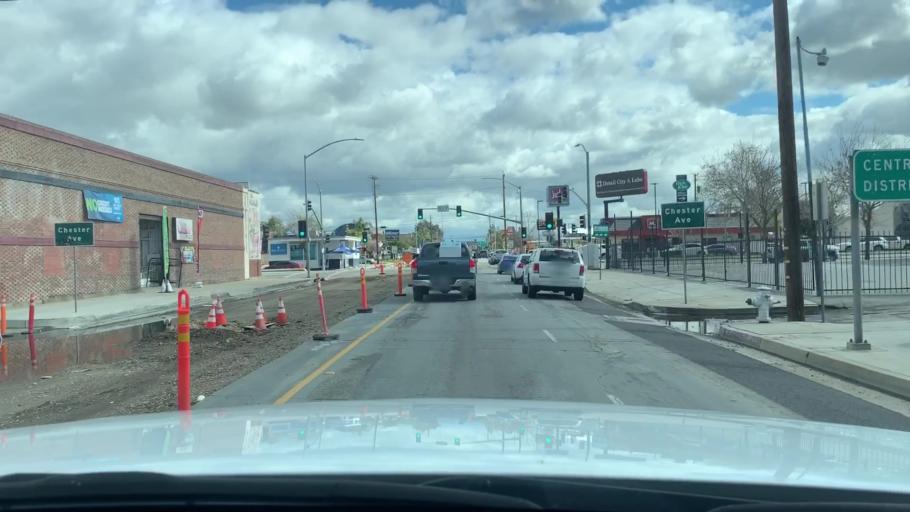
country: US
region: California
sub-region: Kern County
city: Bakersfield
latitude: 35.3801
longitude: -119.0196
